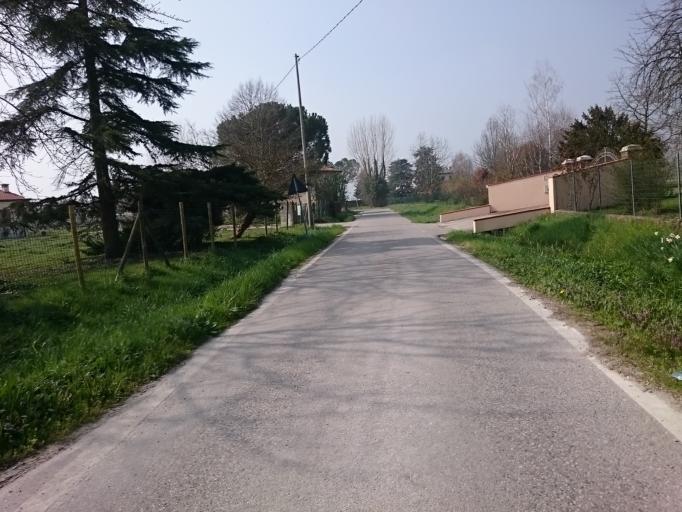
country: IT
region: Veneto
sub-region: Provincia di Padova
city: Pernumia
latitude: 45.2519
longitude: 11.7791
